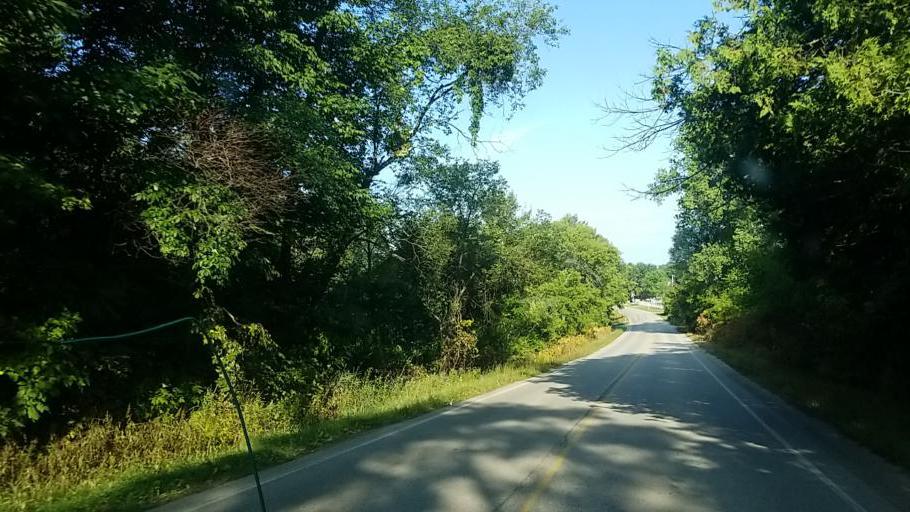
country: US
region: Michigan
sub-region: Newaygo County
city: Fremont
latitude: 43.3462
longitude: -85.9323
